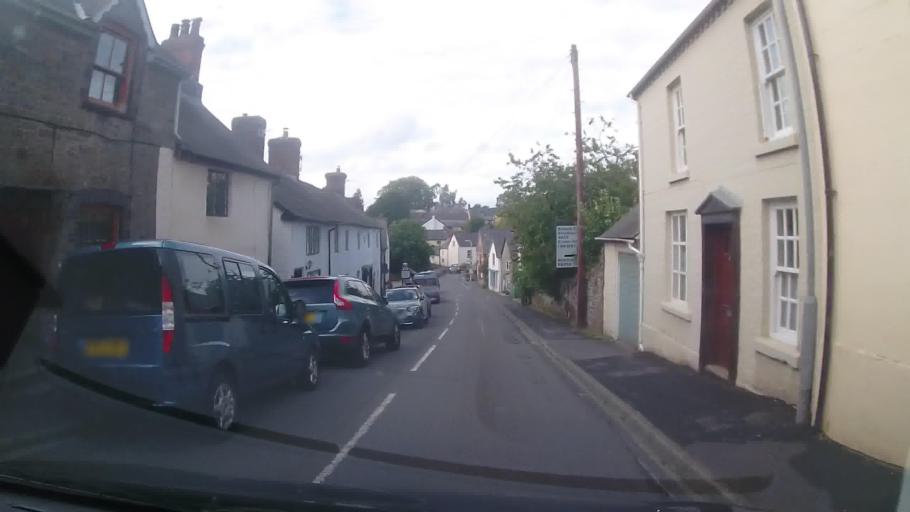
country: GB
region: England
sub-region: Shropshire
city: Acton
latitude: 52.4197
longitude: -3.0301
